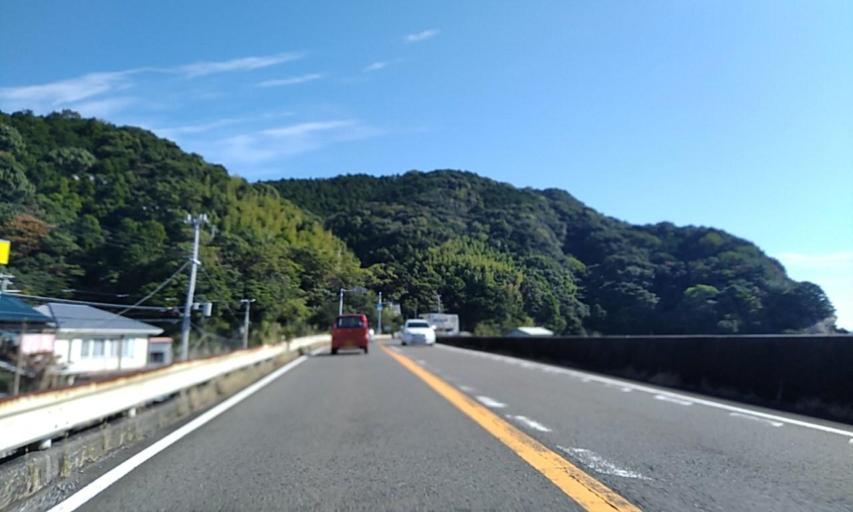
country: JP
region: Mie
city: Owase
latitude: 33.8913
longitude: 136.1071
